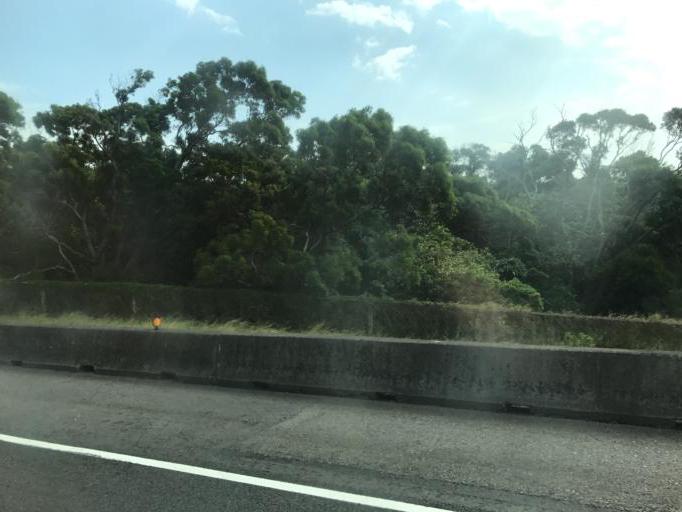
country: TW
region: Taiwan
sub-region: Hsinchu
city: Zhubei
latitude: 24.8767
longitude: 121.0450
